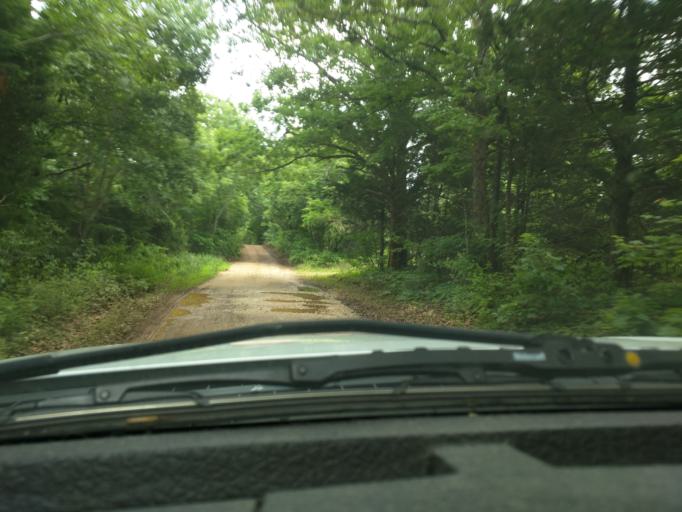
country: US
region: Arkansas
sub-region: Madison County
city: Huntsville
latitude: 35.8887
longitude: -93.5614
